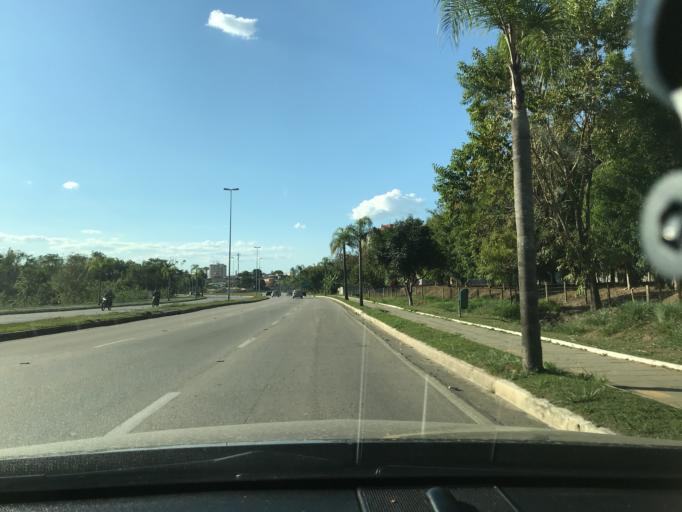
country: BR
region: Sao Paulo
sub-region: Sao Jose Dos Campos
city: Sao Jose dos Campos
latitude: -23.1707
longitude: -45.8950
